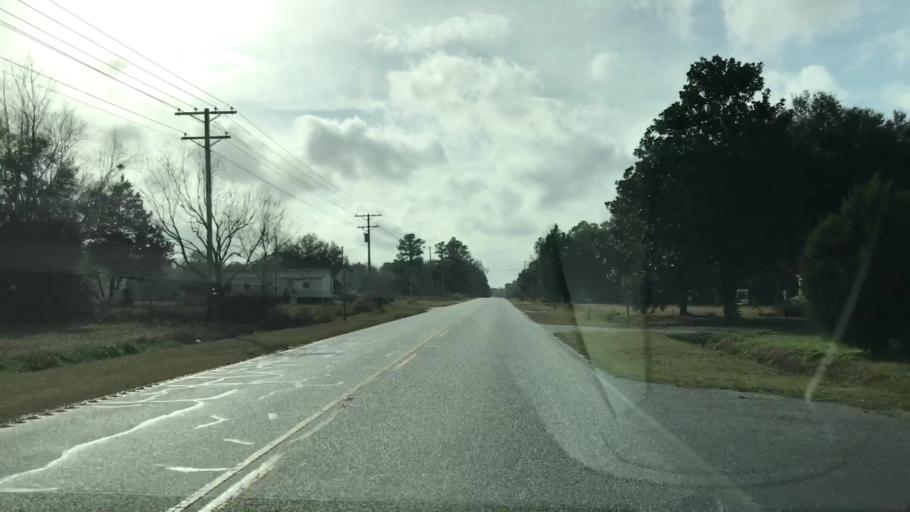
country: US
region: South Carolina
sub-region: Williamsburg County
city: Andrews
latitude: 33.5025
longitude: -79.5265
